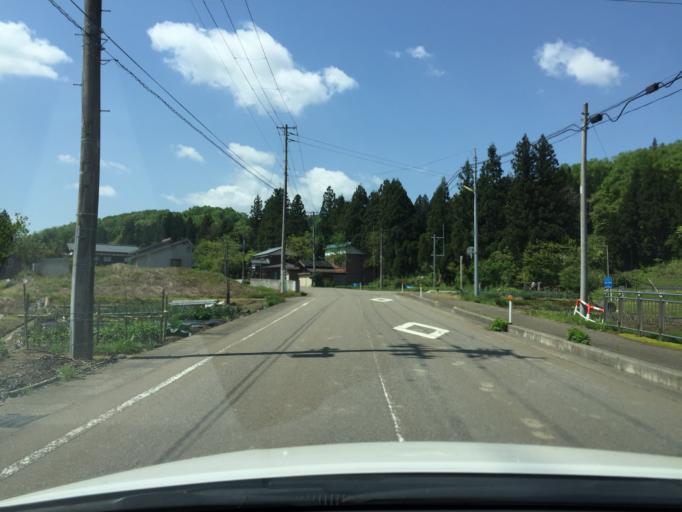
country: JP
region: Niigata
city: Tochio-honcho
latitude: 37.5008
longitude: 139.0576
